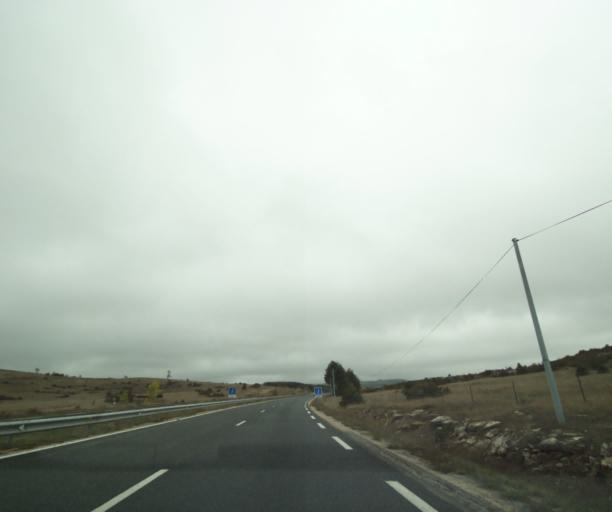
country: FR
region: Midi-Pyrenees
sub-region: Departement de l'Aveyron
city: La Cavalerie
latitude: 44.0362
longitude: 3.1469
